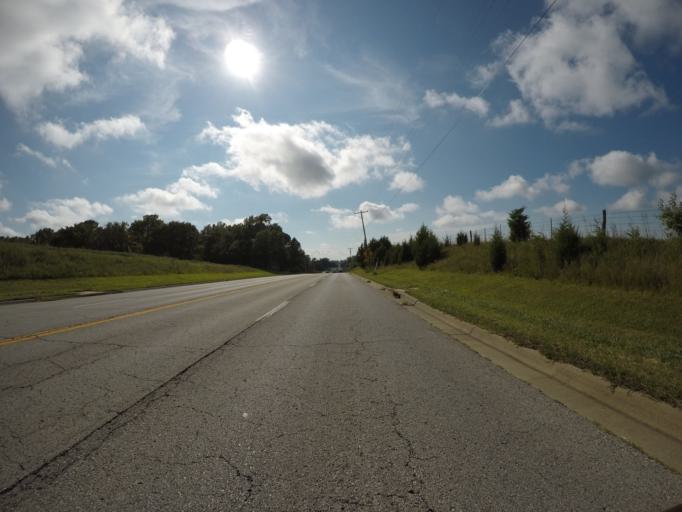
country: US
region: Kansas
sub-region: Leavenworth County
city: Basehor
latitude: 39.1287
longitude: -94.8944
